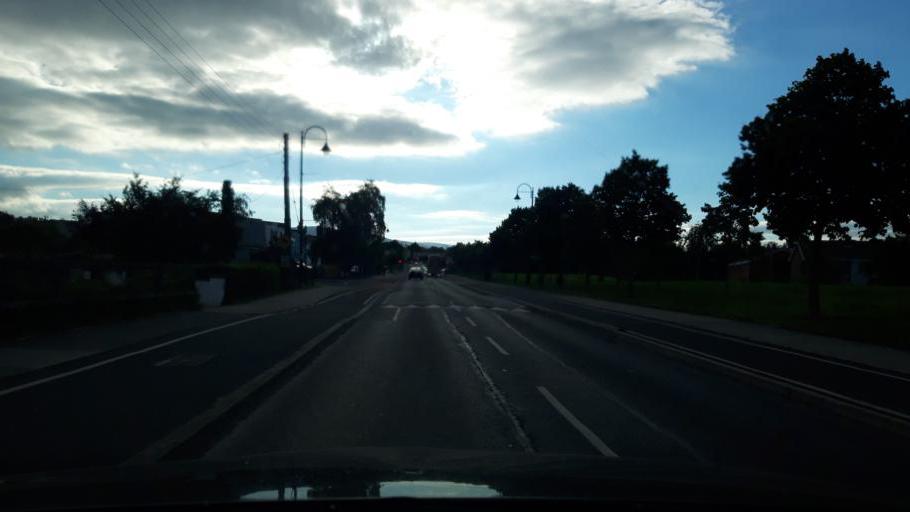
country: IE
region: Leinster
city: Little Bray
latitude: 53.1883
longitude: -6.1195
